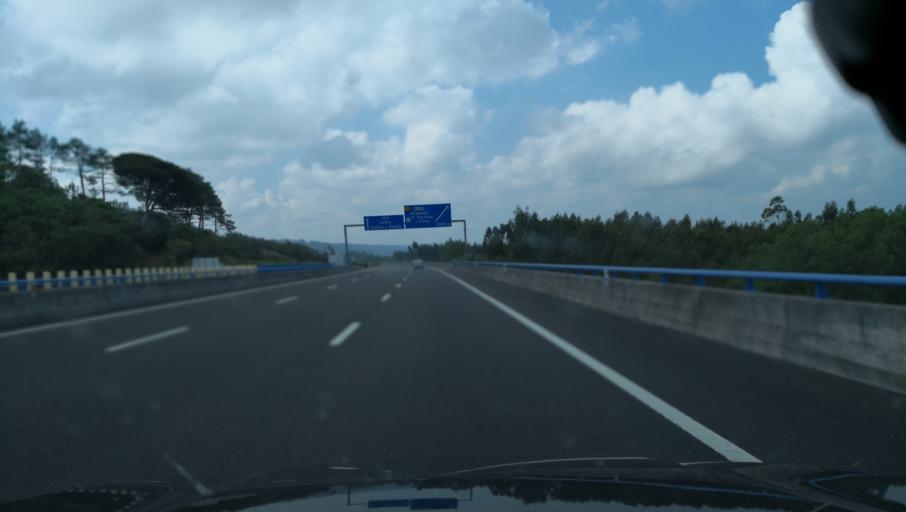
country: PT
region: Leiria
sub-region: Nazare
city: Nazare
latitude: 39.5162
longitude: -9.0873
